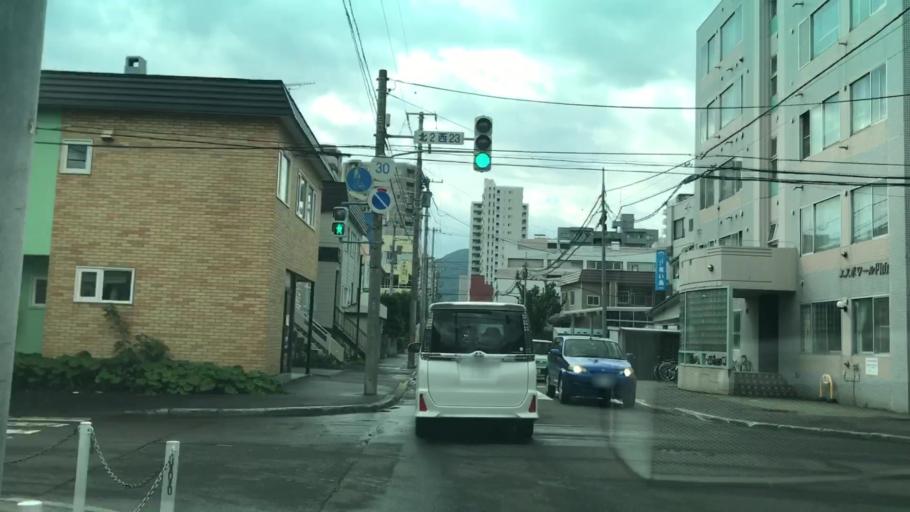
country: JP
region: Hokkaido
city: Sapporo
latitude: 43.0603
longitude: 141.3208
